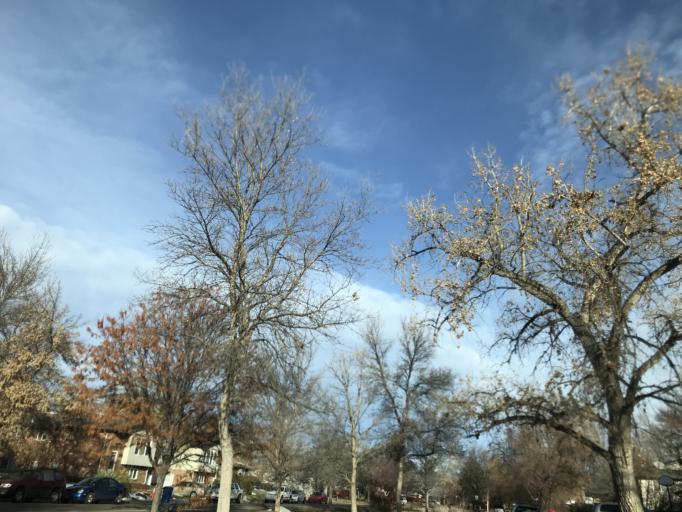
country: US
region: Colorado
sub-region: Arapahoe County
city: Littleton
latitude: 39.6042
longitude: -105.0094
